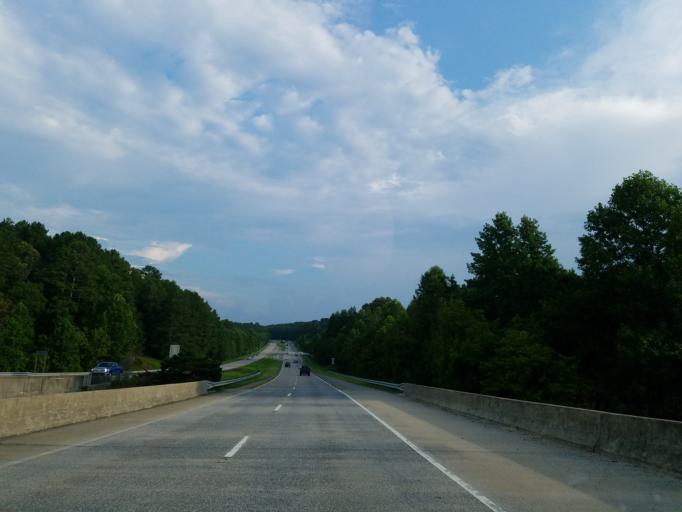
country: US
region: Georgia
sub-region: Pickens County
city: Jasper
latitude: 34.5219
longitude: -84.5186
